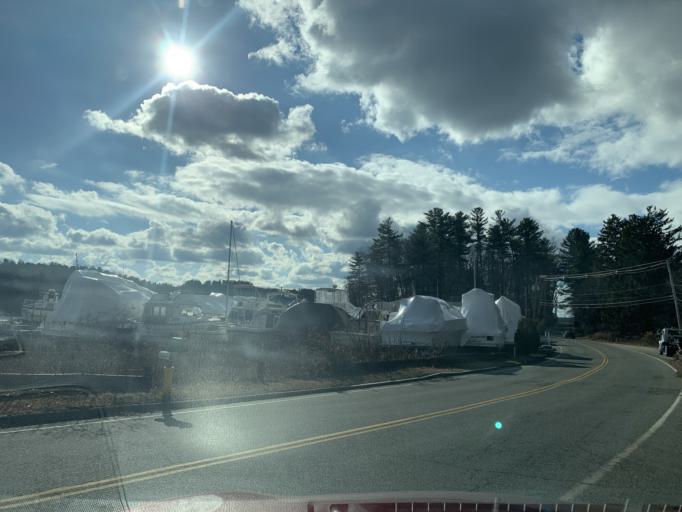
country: US
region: Massachusetts
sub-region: Essex County
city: Amesbury
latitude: 42.8330
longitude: -70.9330
